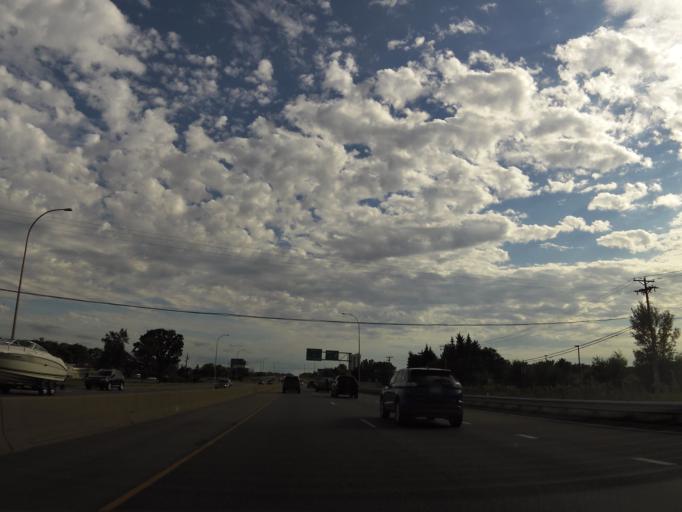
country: US
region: Minnesota
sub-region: Hennepin County
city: New Hope
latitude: 44.9876
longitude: -93.4008
